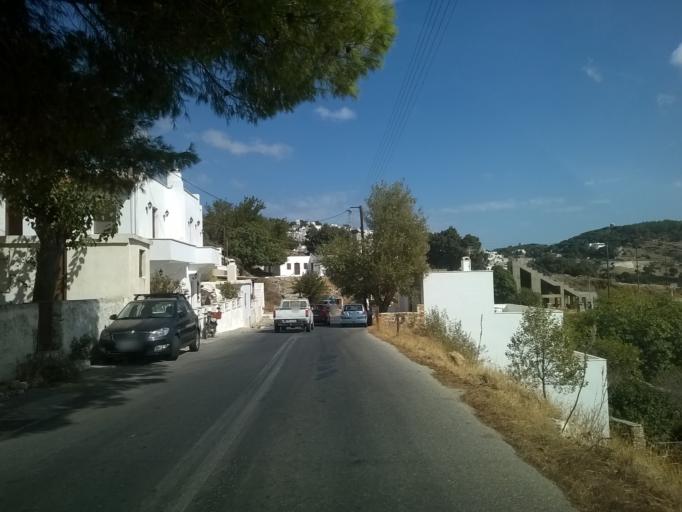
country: GR
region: South Aegean
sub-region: Nomos Kykladon
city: Filotion
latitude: 37.0676
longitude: 25.5166
